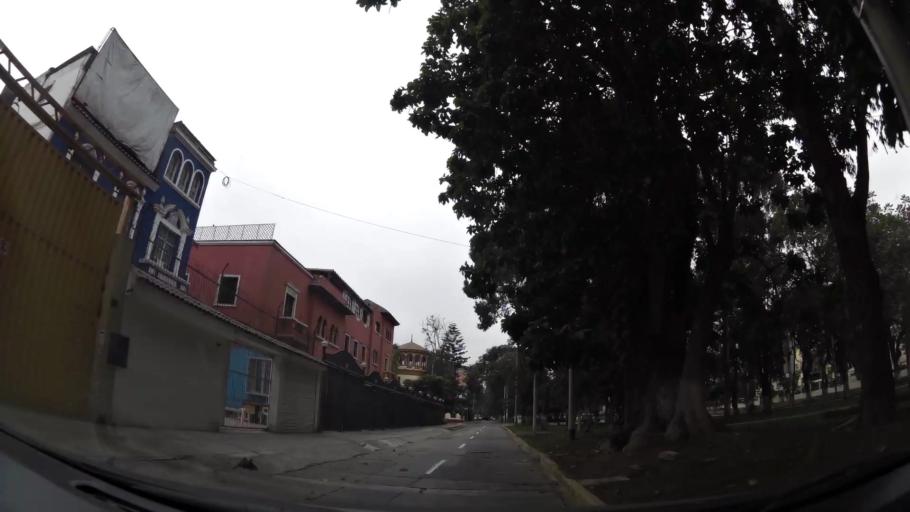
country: PE
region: Lima
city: Lima
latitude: -12.0733
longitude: -77.0421
